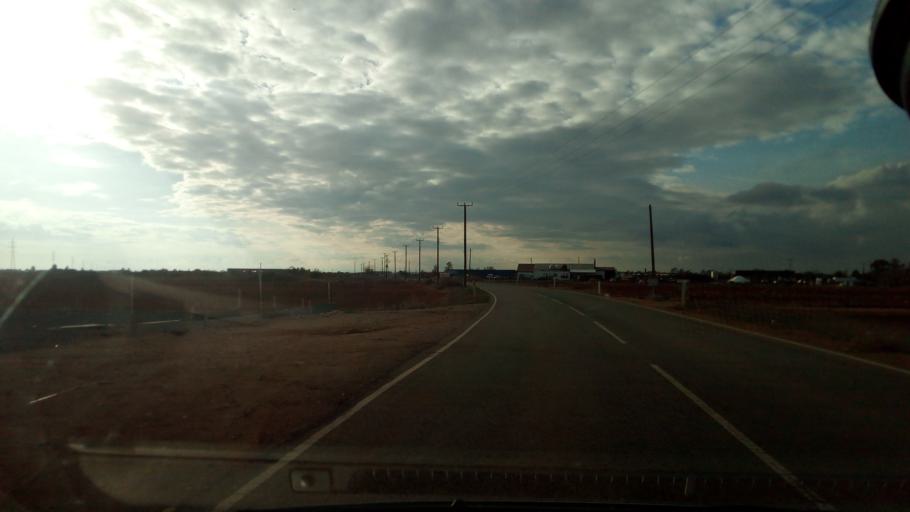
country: CY
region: Ammochostos
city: Avgorou
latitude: 35.0425
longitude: 33.8682
